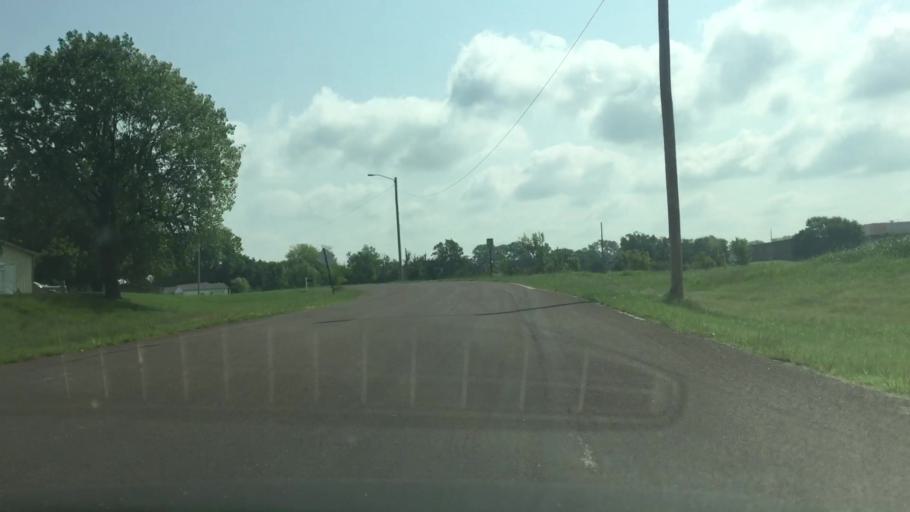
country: US
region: Kansas
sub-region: Allen County
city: Iola
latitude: 37.9041
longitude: -95.4088
